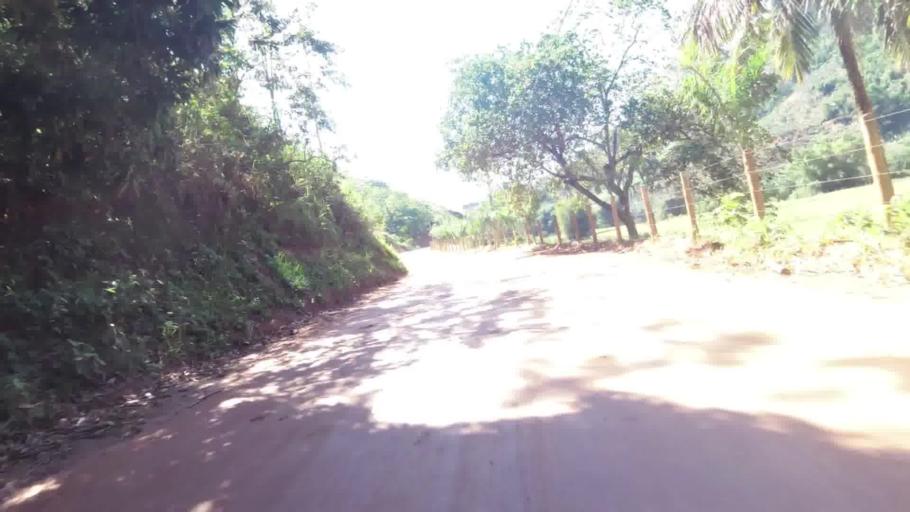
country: BR
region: Espirito Santo
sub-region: Alfredo Chaves
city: Alfredo Chaves
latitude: -20.6364
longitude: -40.7690
